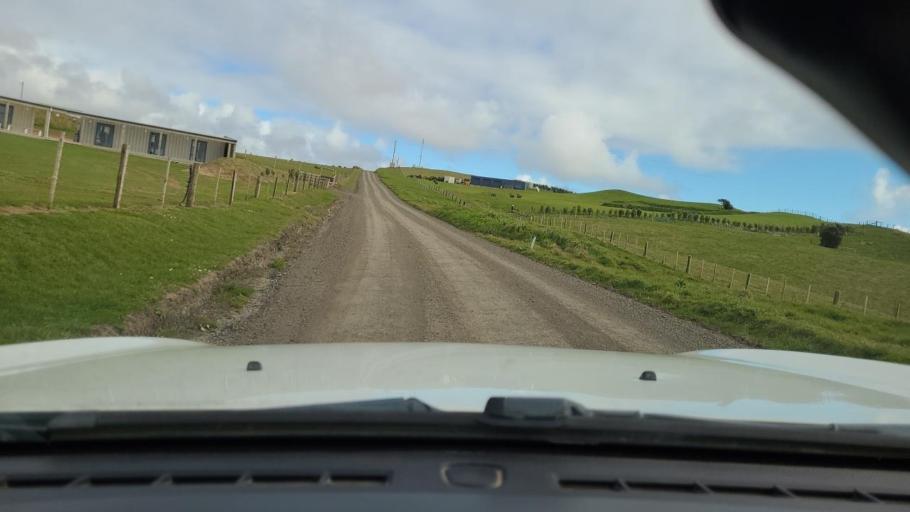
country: NZ
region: Chatham Islands
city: Waitangi
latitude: -43.9588
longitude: -176.5742
